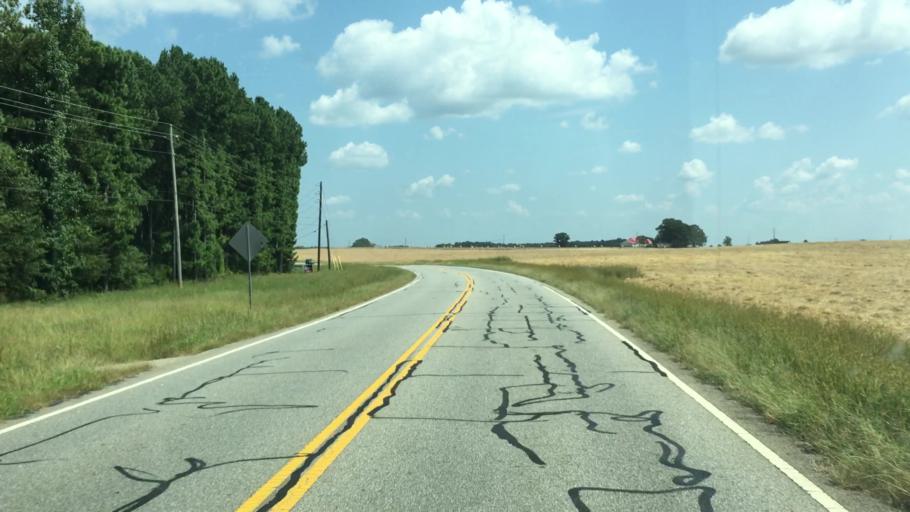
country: US
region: Georgia
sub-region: Oconee County
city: Bogart
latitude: 33.8764
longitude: -83.5370
